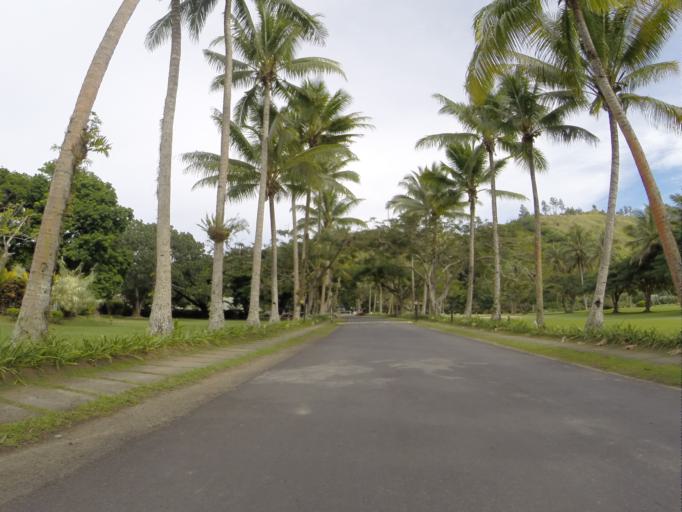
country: FJ
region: Western
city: Nadi
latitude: -18.2013
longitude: 177.6938
